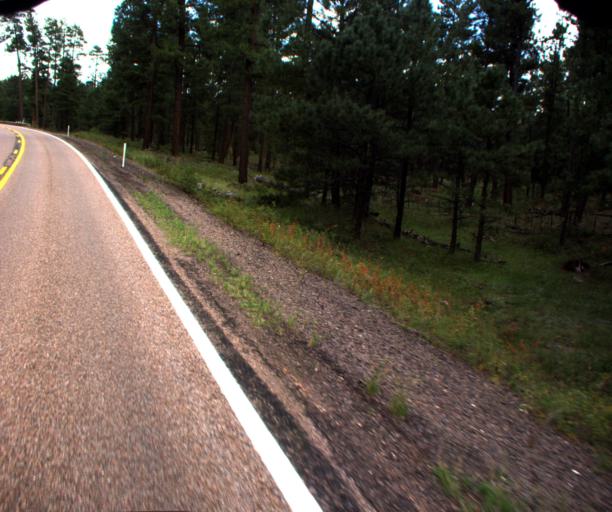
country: US
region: Arizona
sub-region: Navajo County
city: Pinetop-Lakeside
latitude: 34.0532
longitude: -109.7528
